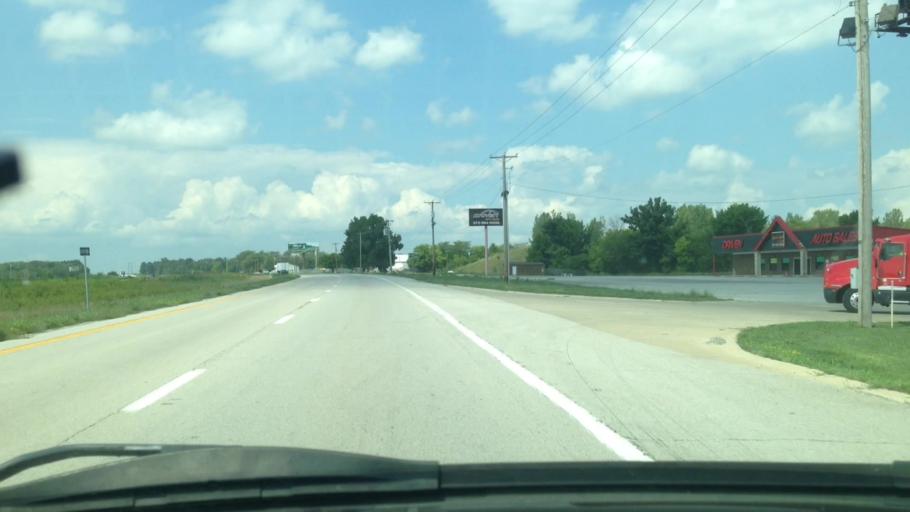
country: US
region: Missouri
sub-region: Lincoln County
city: Troy
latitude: 39.1359
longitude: -90.9644
